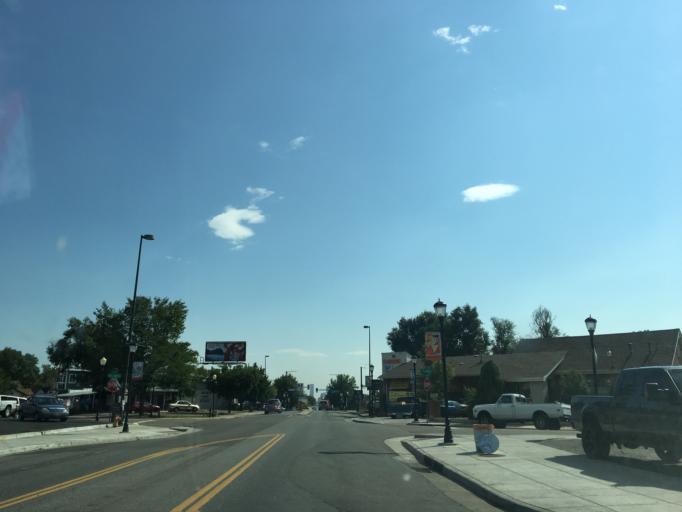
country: US
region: Colorado
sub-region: Jefferson County
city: Lakewood
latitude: 39.7052
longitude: -105.0413
